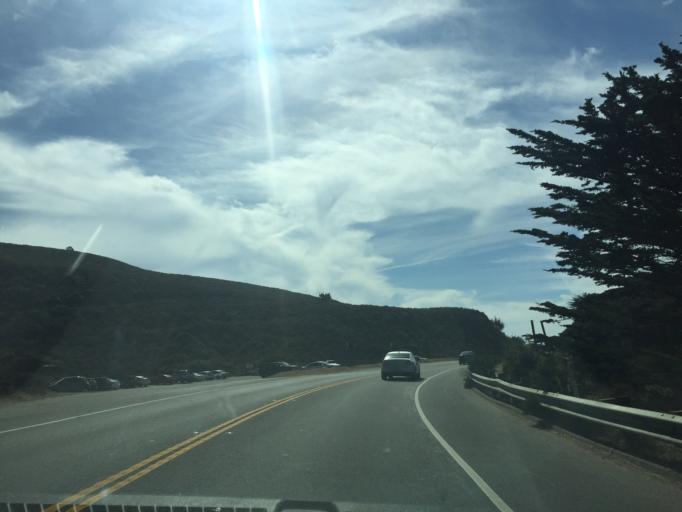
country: US
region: California
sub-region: San Mateo County
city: Montara
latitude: 37.5640
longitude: -122.5126
